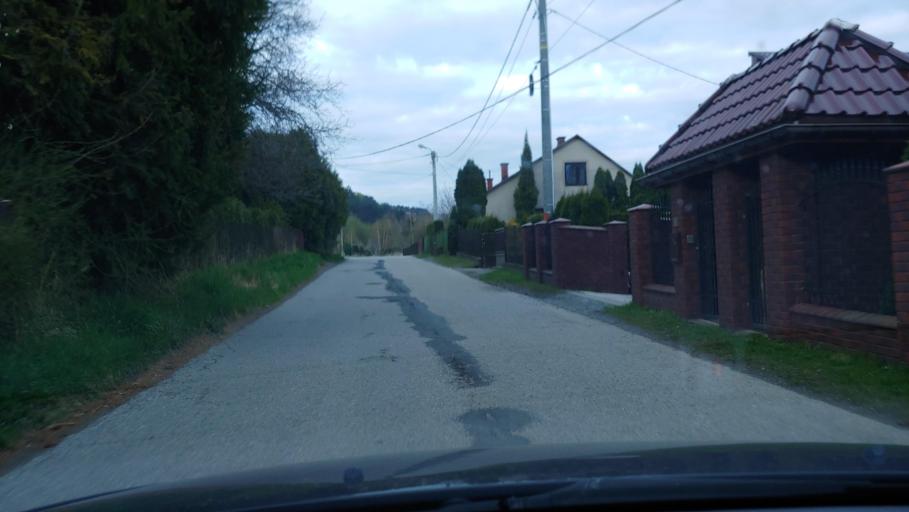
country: PL
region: Lesser Poland Voivodeship
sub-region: Powiat krakowski
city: Bolechowice
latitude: 50.1507
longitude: 19.7646
